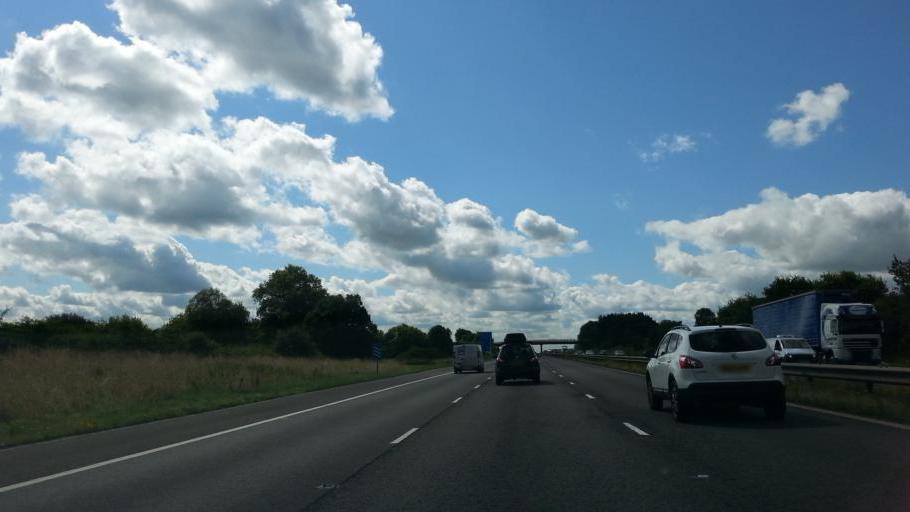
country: GB
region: England
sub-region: Leicestershire
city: Markfield
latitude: 52.7079
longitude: -1.2917
